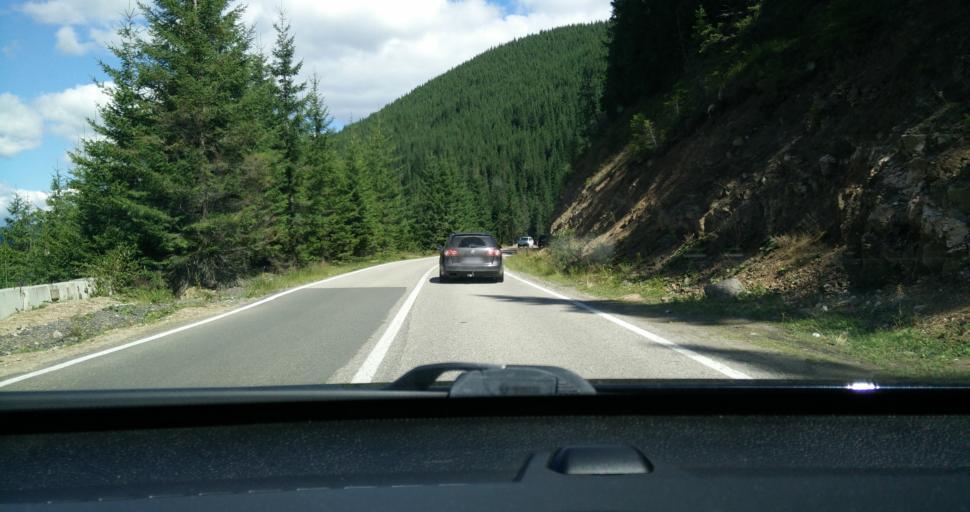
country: RO
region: Alba
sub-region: Comuna Sugag
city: Sugag
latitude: 45.5422
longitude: 23.6376
